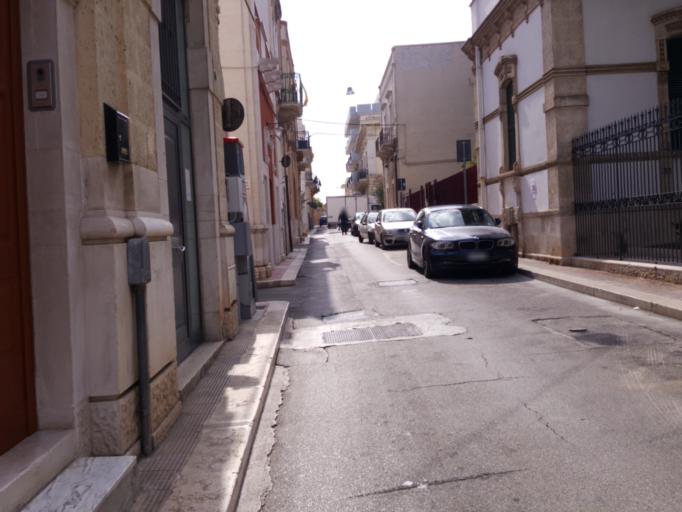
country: IT
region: Apulia
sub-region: Provincia di Bari
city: Triggiano
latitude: 41.0621
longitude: 16.9245
